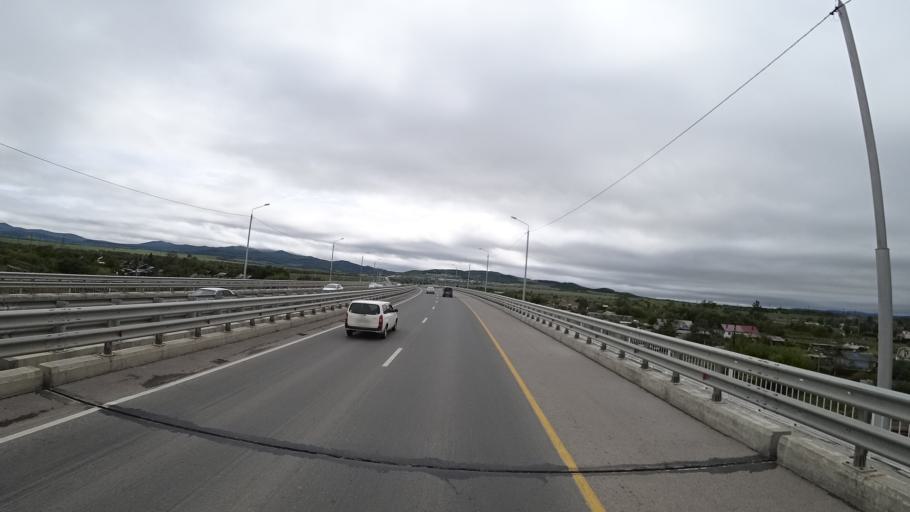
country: RU
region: Primorskiy
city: Monastyrishche
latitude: 44.1918
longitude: 132.4419
